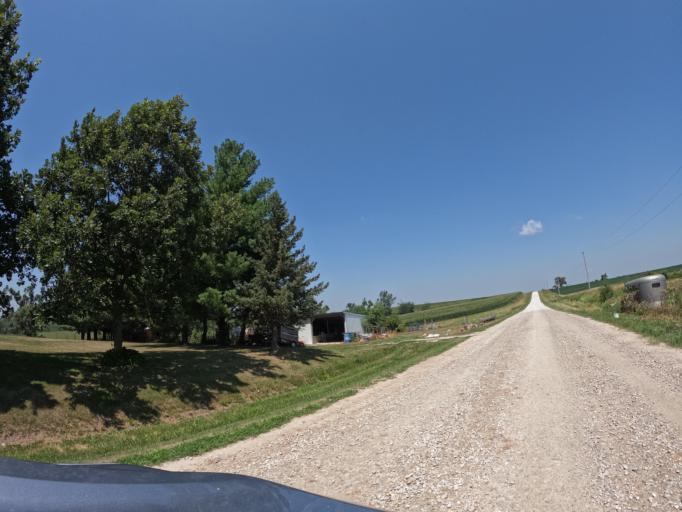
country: US
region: Iowa
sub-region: Keokuk County
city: Sigourney
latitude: 41.2611
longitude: -92.1697
